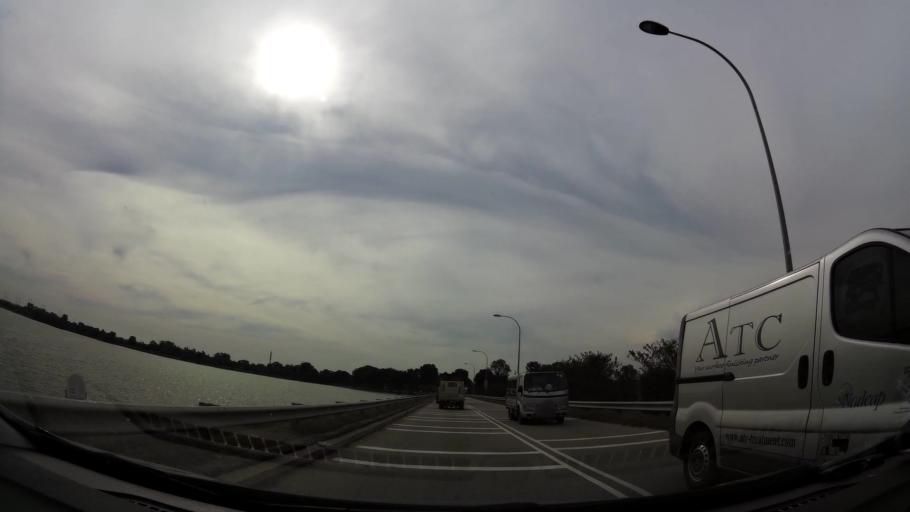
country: MY
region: Johor
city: Johor Bahru
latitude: 1.4386
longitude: 103.7410
